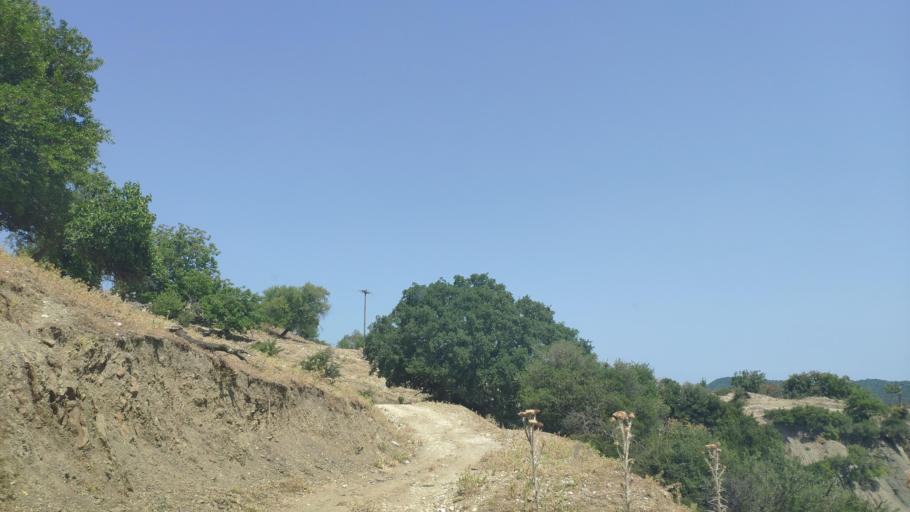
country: GR
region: West Greece
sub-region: Nomos Aitolias kai Akarnanias
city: Monastirakion
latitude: 38.8160
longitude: 21.0175
